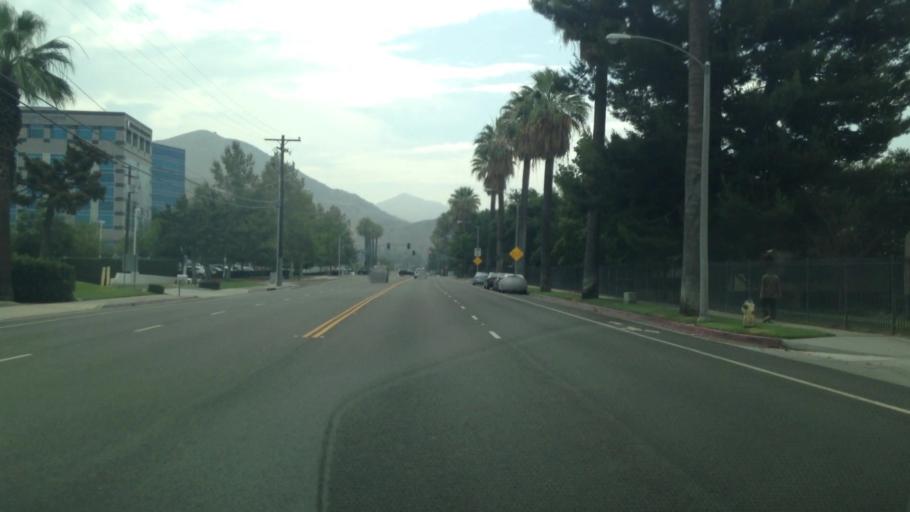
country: US
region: California
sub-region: Riverside County
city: Highgrove
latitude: 33.9903
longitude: -117.3425
